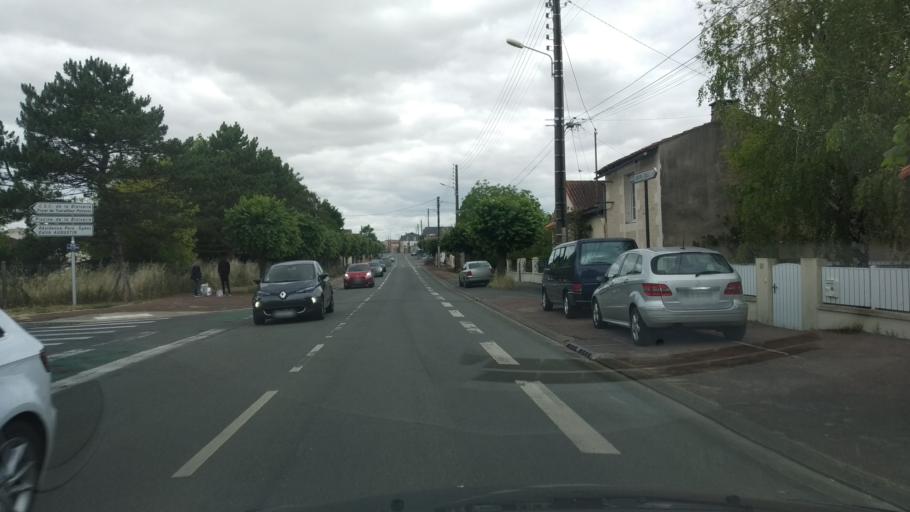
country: FR
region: Poitou-Charentes
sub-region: Departement de la Vienne
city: Poitiers
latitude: 46.5950
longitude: 0.3278
